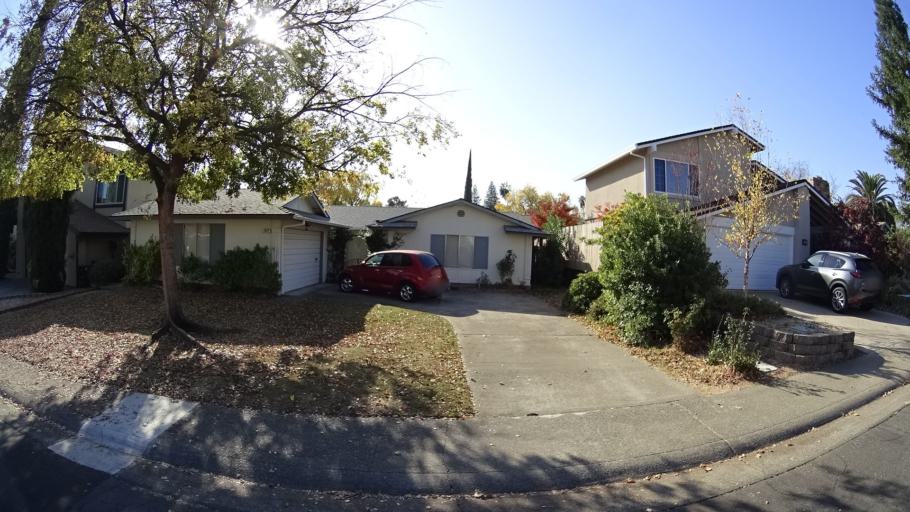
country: US
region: California
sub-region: Sacramento County
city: Fair Oaks
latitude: 38.6722
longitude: -121.2781
